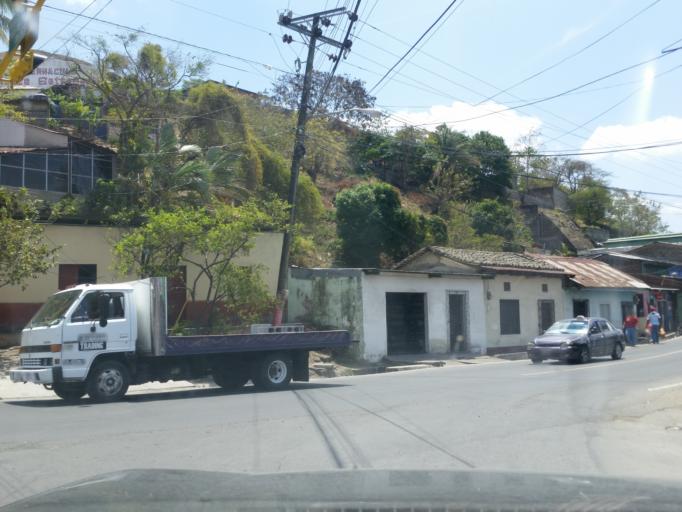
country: NI
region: Boaco
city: Boaco
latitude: 12.4677
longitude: -85.6584
